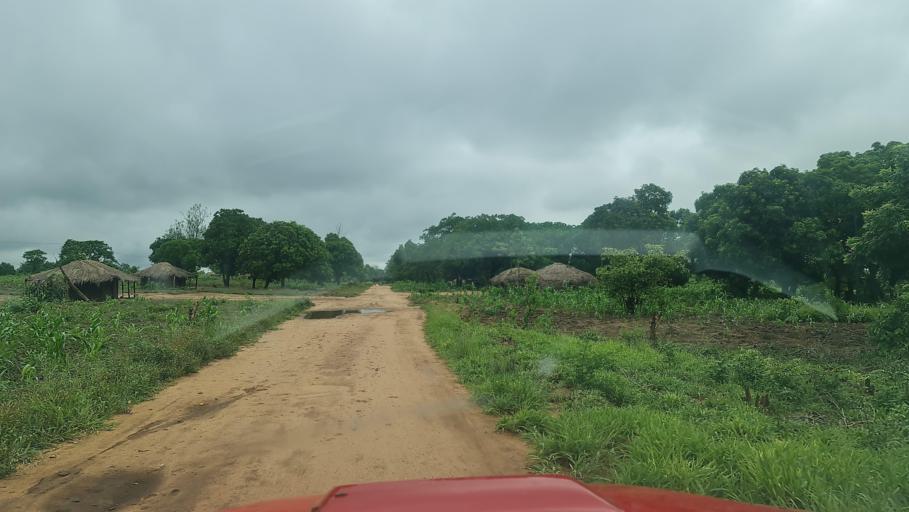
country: MW
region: Southern Region
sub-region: Nsanje District
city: Nsanje
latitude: -17.1791
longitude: 35.8963
